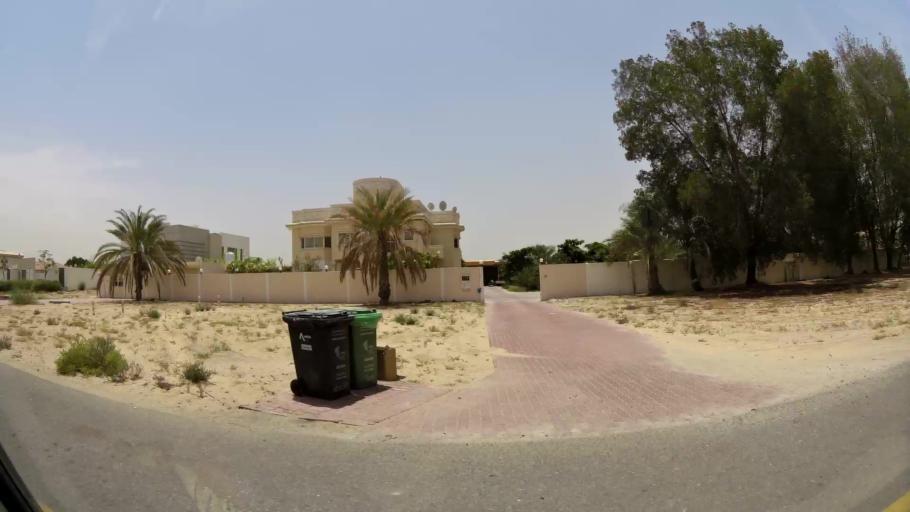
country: AE
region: Ash Shariqah
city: Sharjah
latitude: 25.2462
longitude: 55.4684
